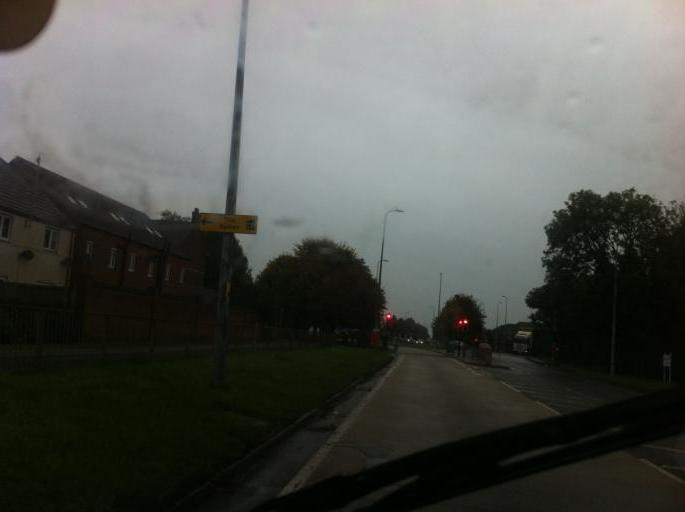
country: GB
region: England
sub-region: Lincolnshire
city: Kirton
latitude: 52.9262
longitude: -0.0545
